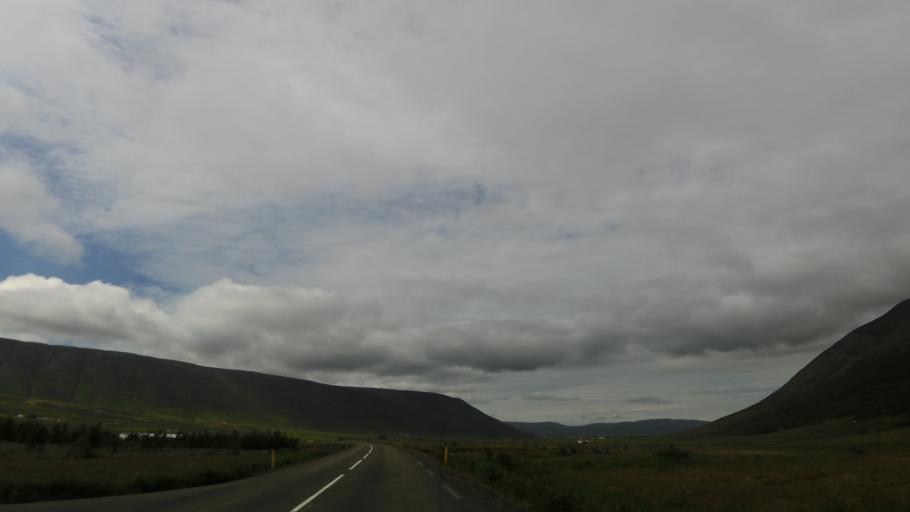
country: IS
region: Northeast
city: Laugar
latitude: 65.7153
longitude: -17.7278
